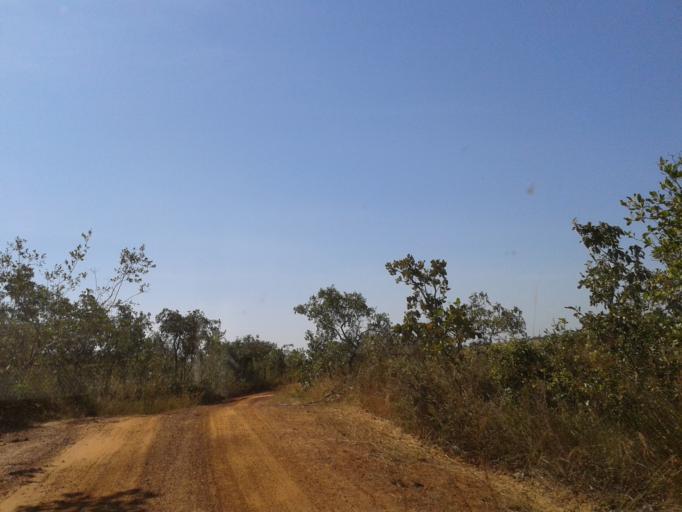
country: BR
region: Minas Gerais
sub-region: Campina Verde
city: Campina Verde
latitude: -19.4411
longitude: -49.5796
